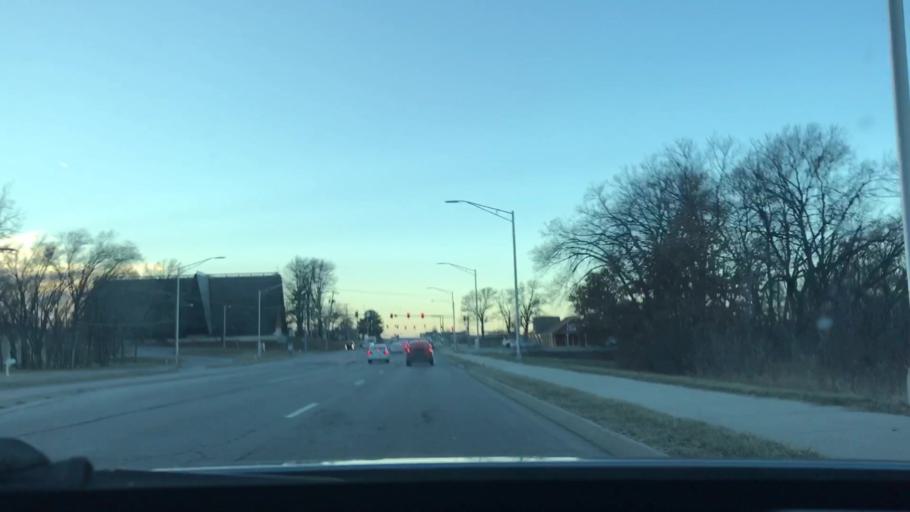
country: US
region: Kansas
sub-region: Wyandotte County
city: Edwardsville
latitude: 39.1165
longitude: -94.7956
